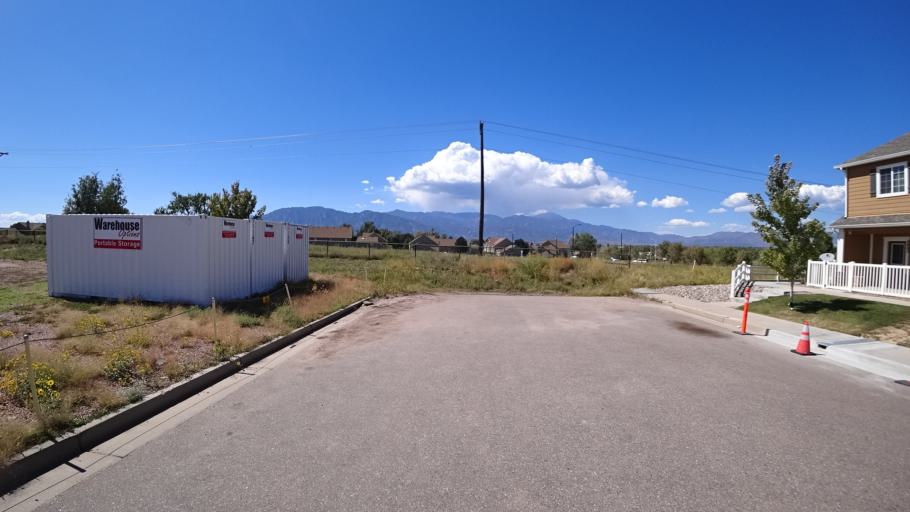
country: US
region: Colorado
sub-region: El Paso County
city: Stratmoor
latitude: 38.7862
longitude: -104.7384
